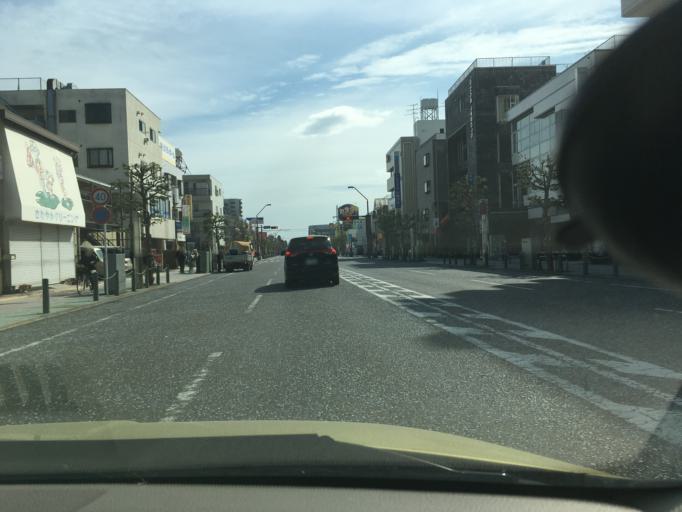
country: JP
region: Kanagawa
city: Zama
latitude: 35.5737
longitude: 139.3672
